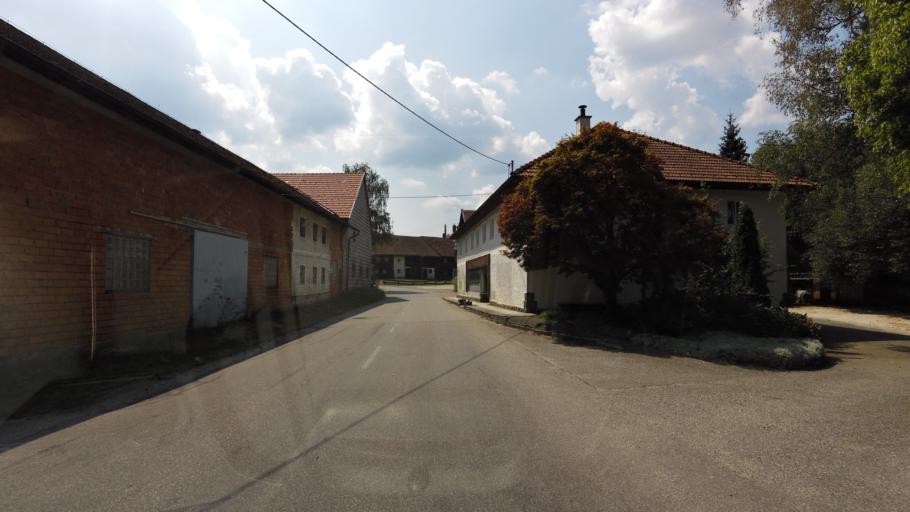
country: AT
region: Upper Austria
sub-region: Politischer Bezirk Ried im Innkreis
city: Waldzell
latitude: 48.1239
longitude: 13.4148
